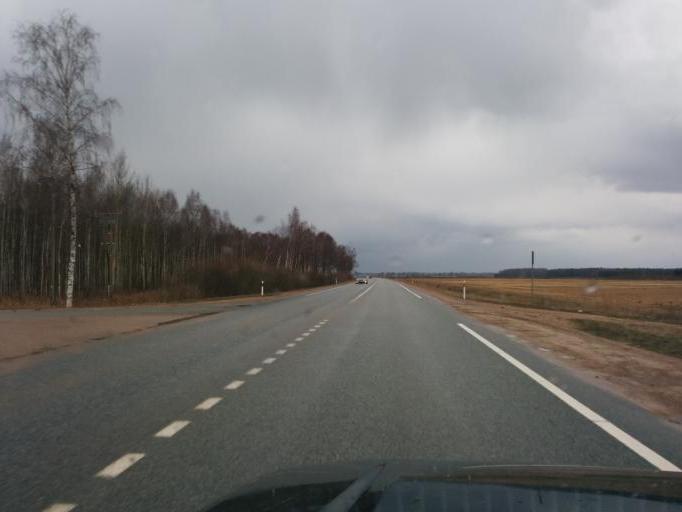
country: LV
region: Marupe
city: Marupe
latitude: 56.8557
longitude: 23.9984
